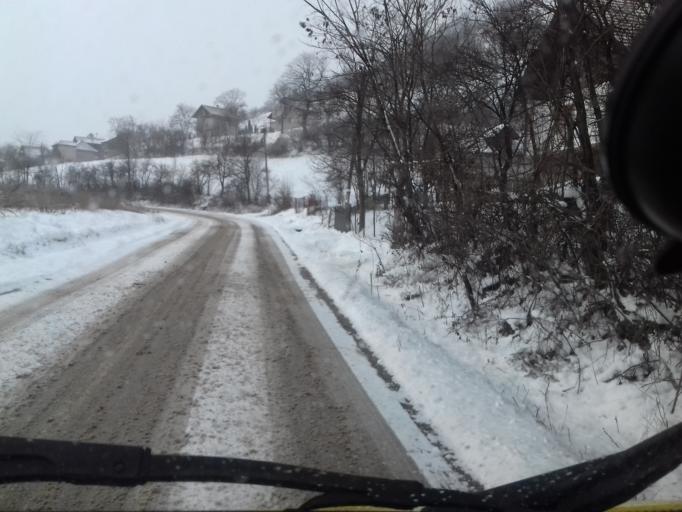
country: BA
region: Federation of Bosnia and Herzegovina
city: Zenica
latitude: 44.2431
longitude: 17.8958
